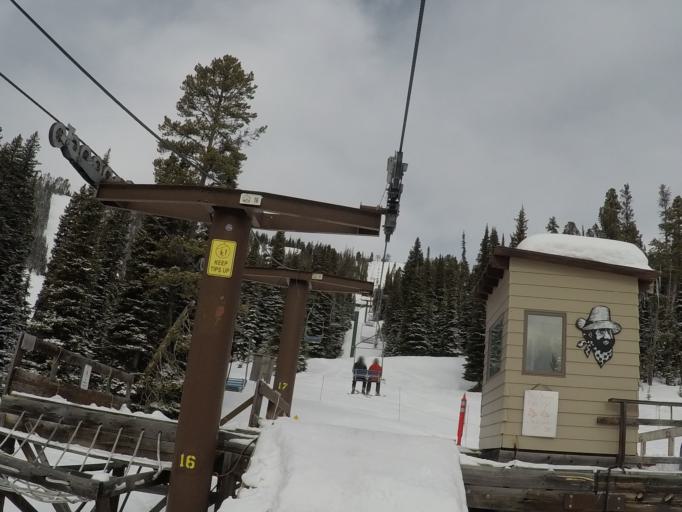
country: US
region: Montana
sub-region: Meagher County
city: White Sulphur Springs
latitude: 46.8339
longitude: -110.7101
